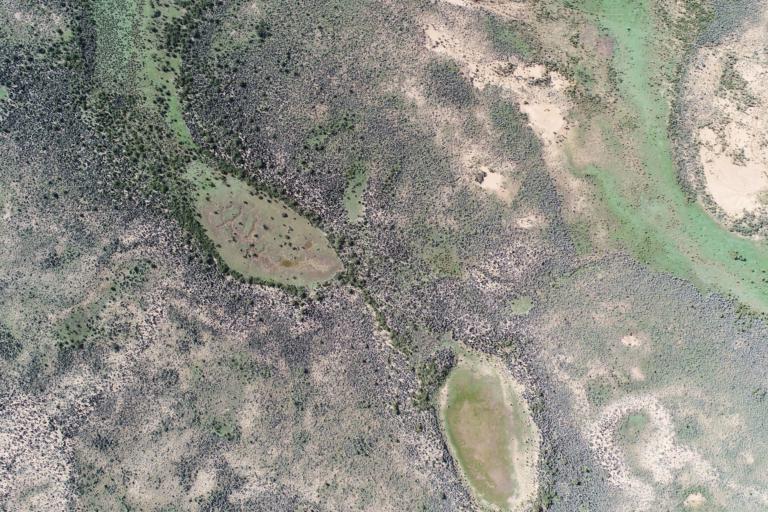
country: BO
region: La Paz
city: Curahuara de Carangas
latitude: -17.3021
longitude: -68.5093
